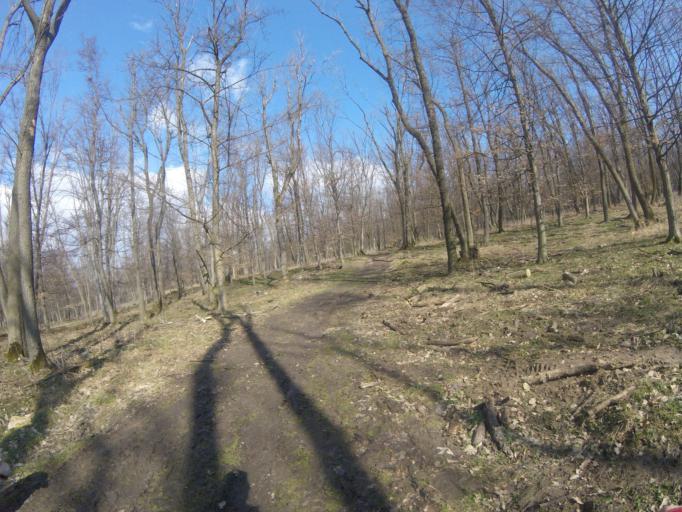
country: HU
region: Komarom-Esztergom
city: Tardos
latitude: 47.6752
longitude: 18.4782
